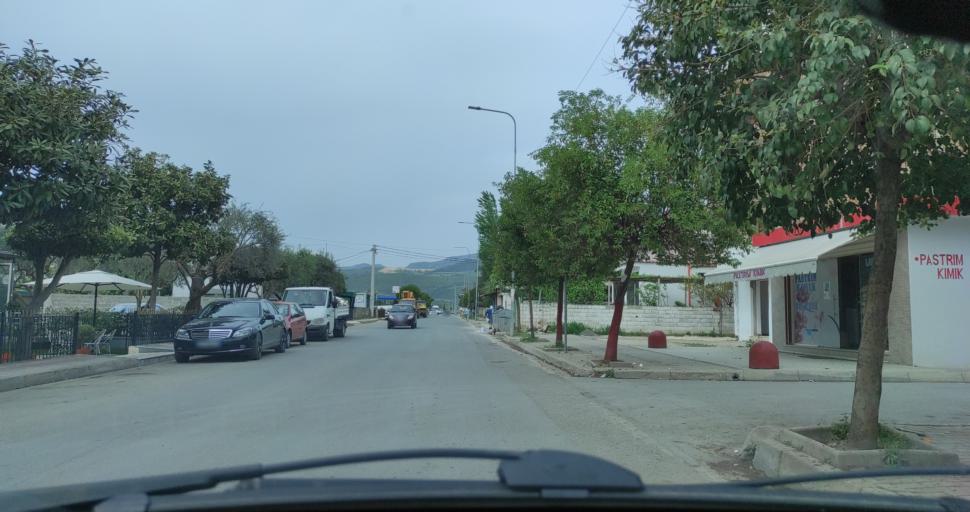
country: AL
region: Durres
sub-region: Rrethi i Krujes
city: Fushe-Kruje
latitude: 41.4812
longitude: 19.7222
